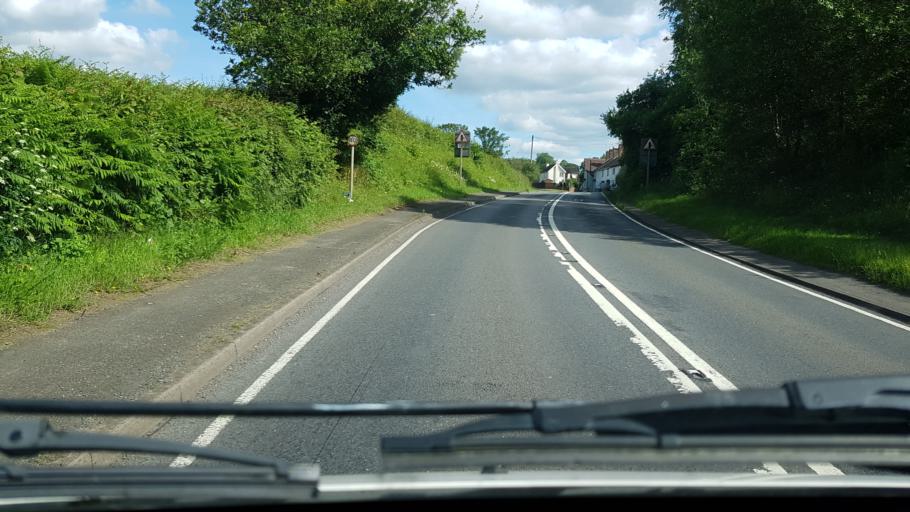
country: GB
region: England
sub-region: Shropshire
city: Romsley
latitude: 52.4290
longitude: -2.3095
